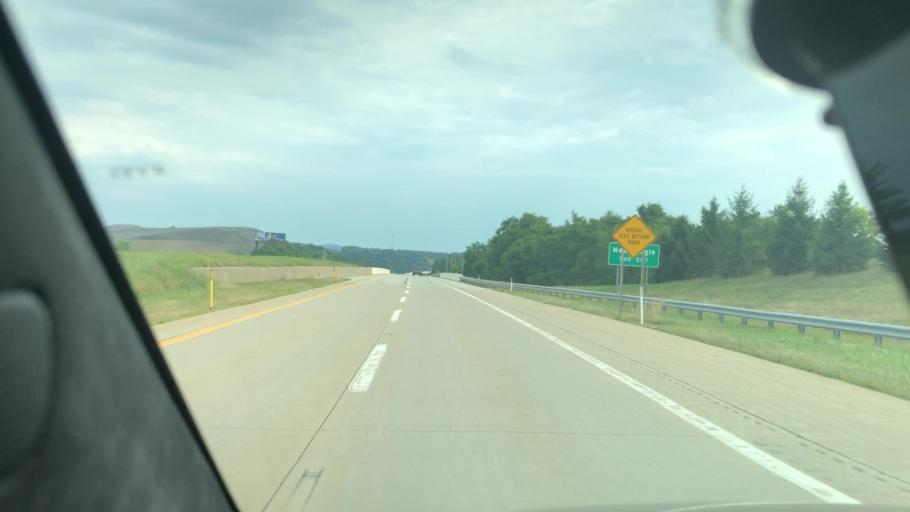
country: US
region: Pennsylvania
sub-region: Washington County
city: Gastonville
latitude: 40.2266
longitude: -79.9857
